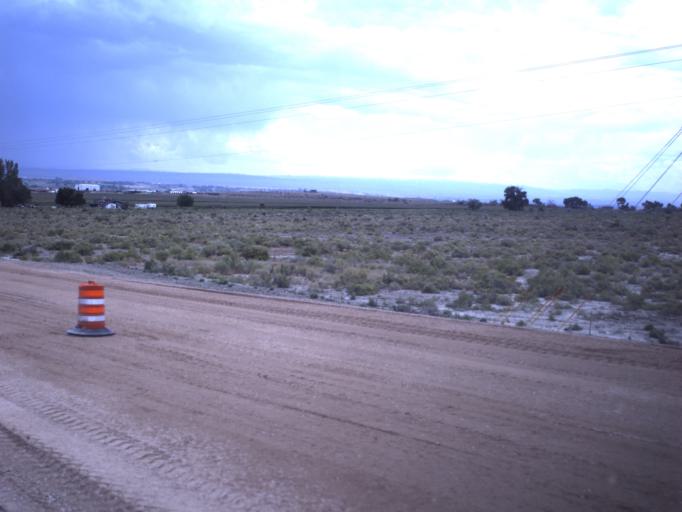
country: US
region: Utah
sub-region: Duchesne County
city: Roosevelt
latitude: 40.2292
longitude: -110.0675
